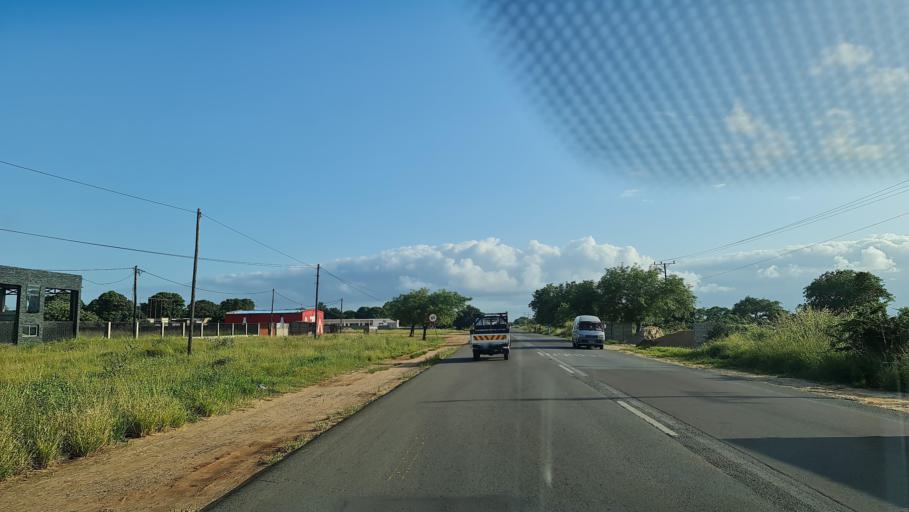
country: MZ
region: Maputo City
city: Maputo
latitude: -25.6873
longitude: 32.6649
